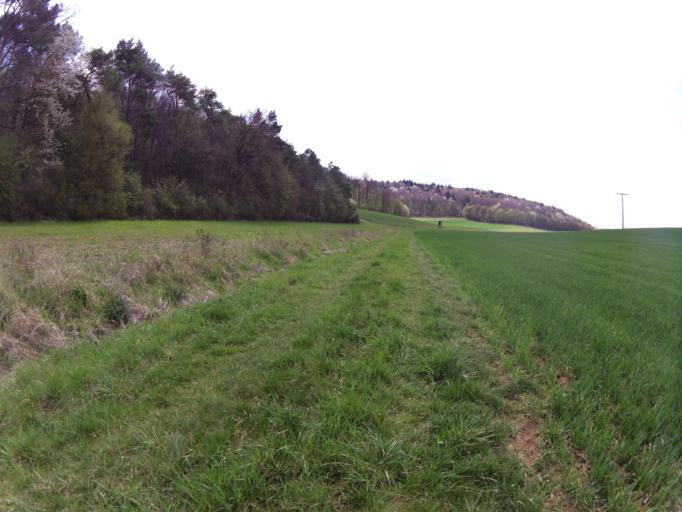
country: DE
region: Bavaria
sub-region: Regierungsbezirk Unterfranken
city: Greussenheim
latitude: 49.7960
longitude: 9.7849
